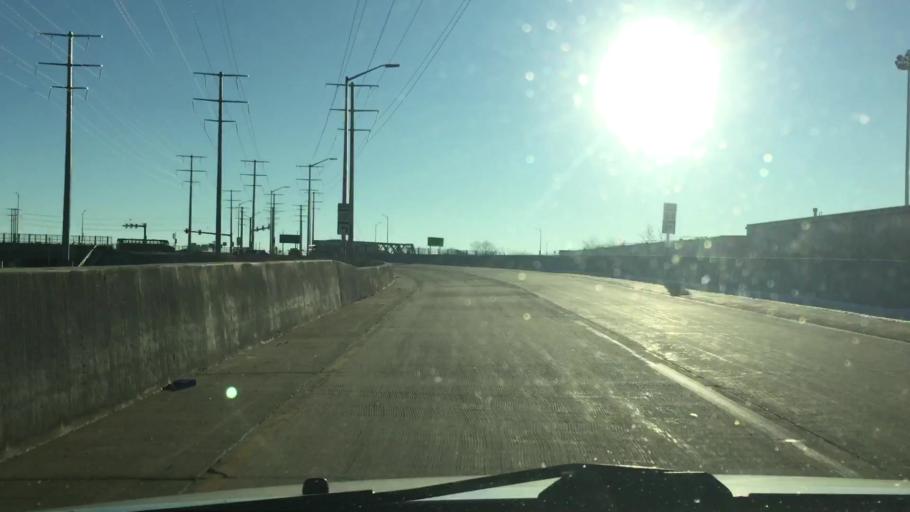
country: US
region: Wisconsin
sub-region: Waukesha County
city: Elm Grove
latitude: 43.0288
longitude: -88.0497
